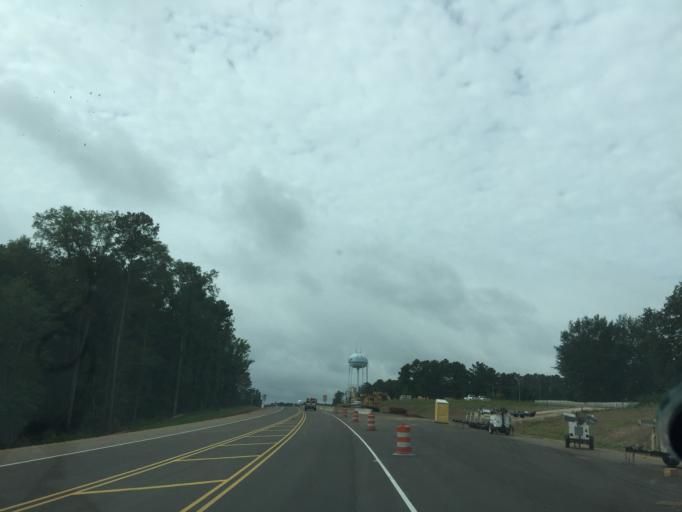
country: US
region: Mississippi
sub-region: Rankin County
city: Brandon
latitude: 32.2821
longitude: -89.9931
